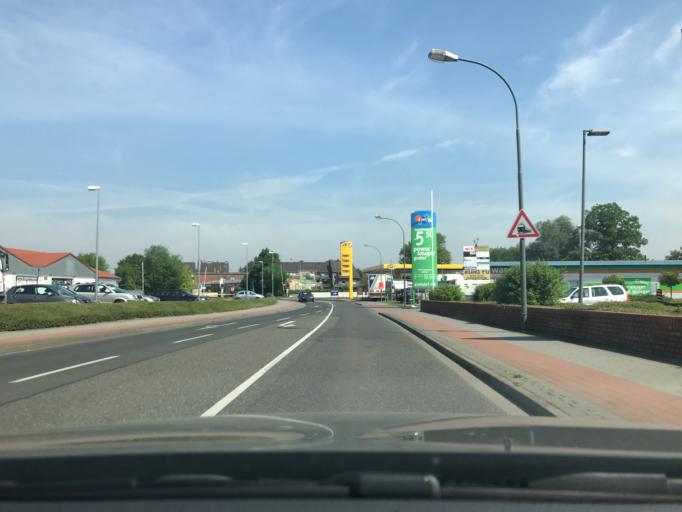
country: DE
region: North Rhine-Westphalia
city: Tonisvorst
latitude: 51.3194
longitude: 6.5050
